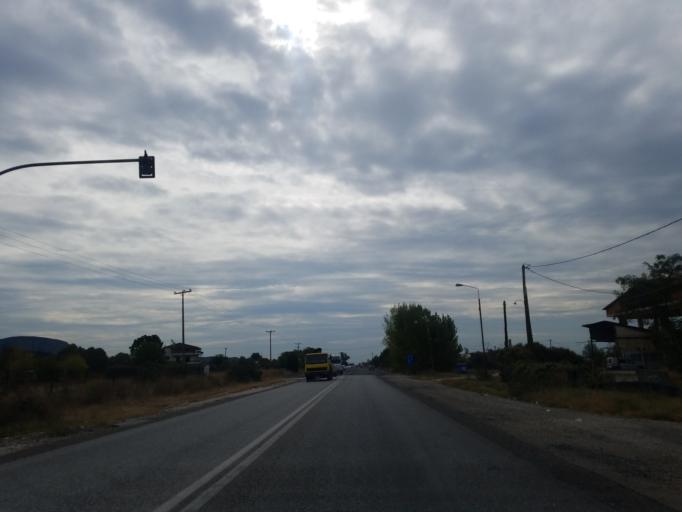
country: GR
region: Thessaly
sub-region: Trikala
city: Kalampaka
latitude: 39.6901
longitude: 21.6460
